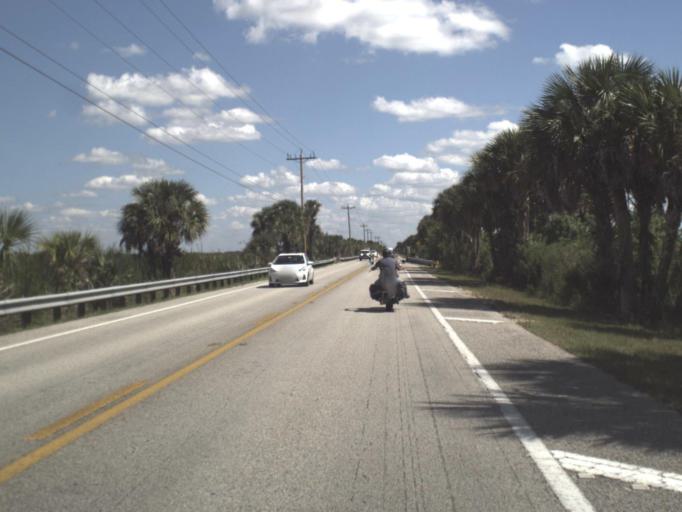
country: US
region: Florida
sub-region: Collier County
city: Marco
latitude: 25.9296
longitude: -81.4364
